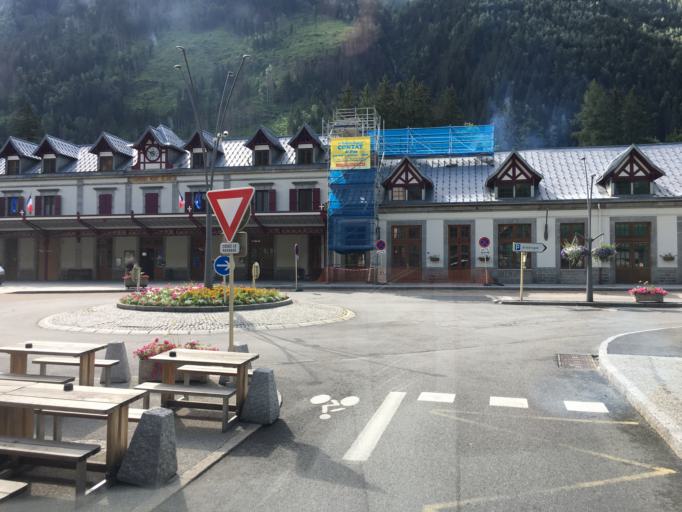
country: FR
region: Rhone-Alpes
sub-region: Departement de la Haute-Savoie
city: Chamonix-Mont-Blanc
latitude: 45.9230
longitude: 6.8732
